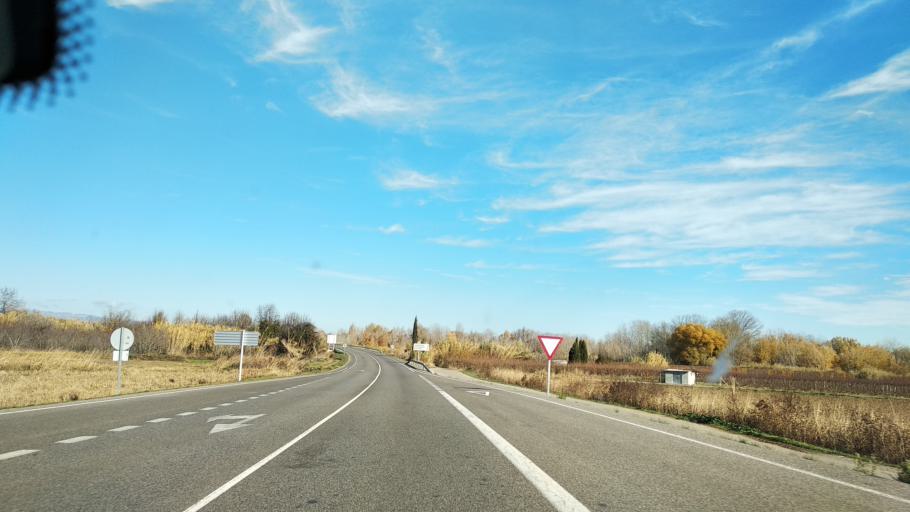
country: ES
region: Catalonia
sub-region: Provincia de Lleida
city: Corbins
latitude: 41.6846
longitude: 0.6979
